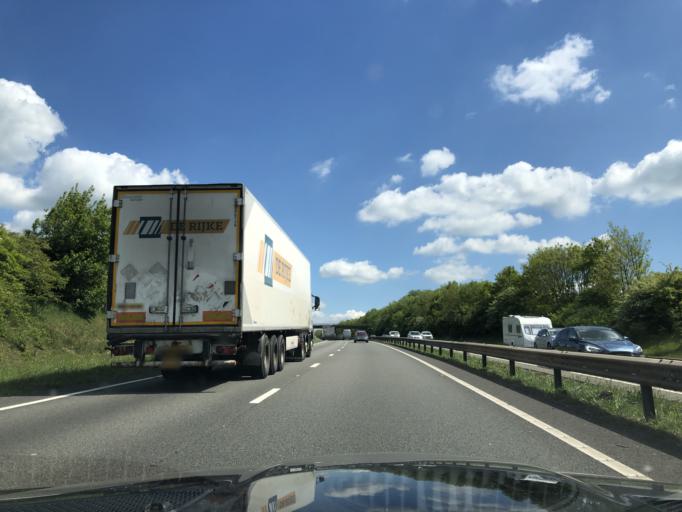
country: GB
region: England
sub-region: Northamptonshire
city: Brixworth
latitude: 52.4007
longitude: -0.9296
